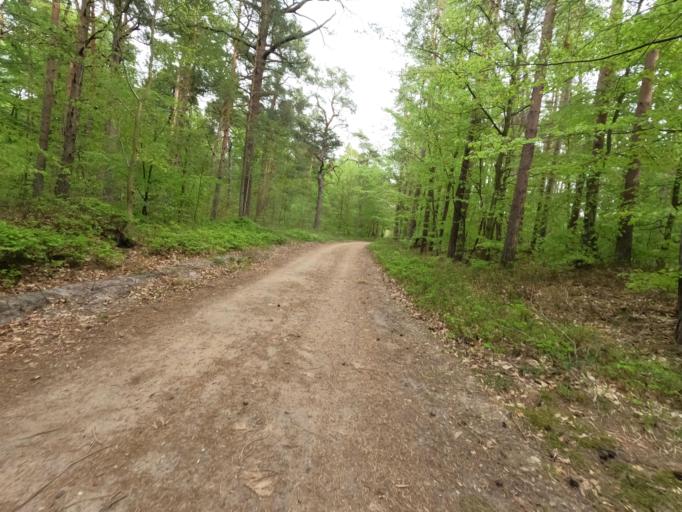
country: DE
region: Mecklenburg-Vorpommern
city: Ostseebad Prerow
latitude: 54.4458
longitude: 12.5461
